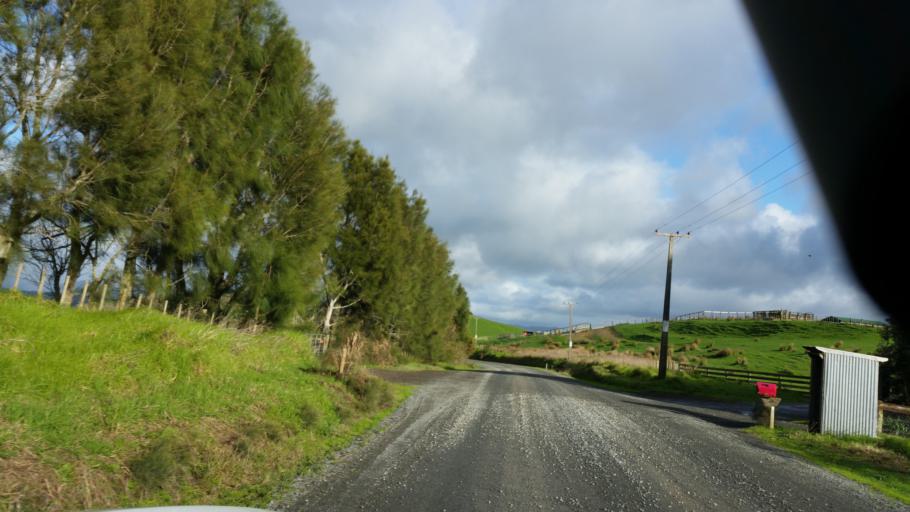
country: NZ
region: Northland
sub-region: Whangarei
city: Maungatapere
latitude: -35.7026
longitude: 174.0907
